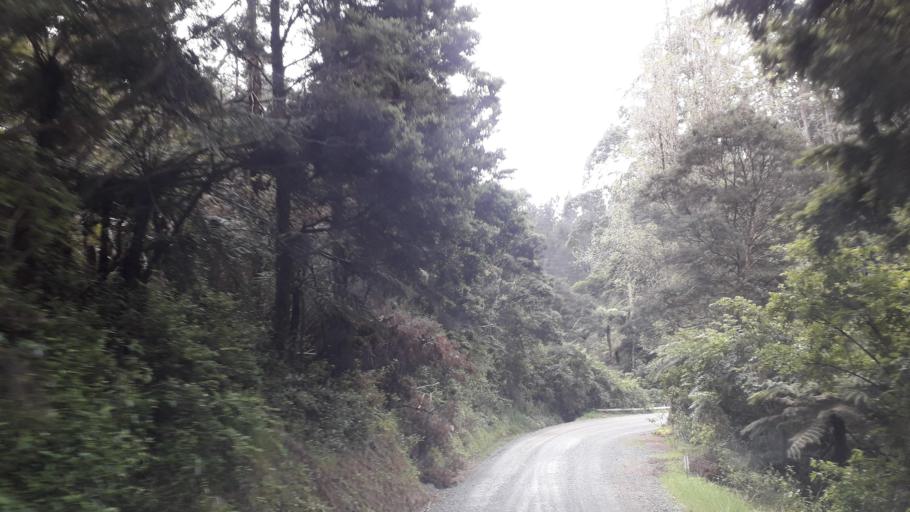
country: NZ
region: Northland
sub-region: Far North District
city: Taipa
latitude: -35.0647
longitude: 173.5489
